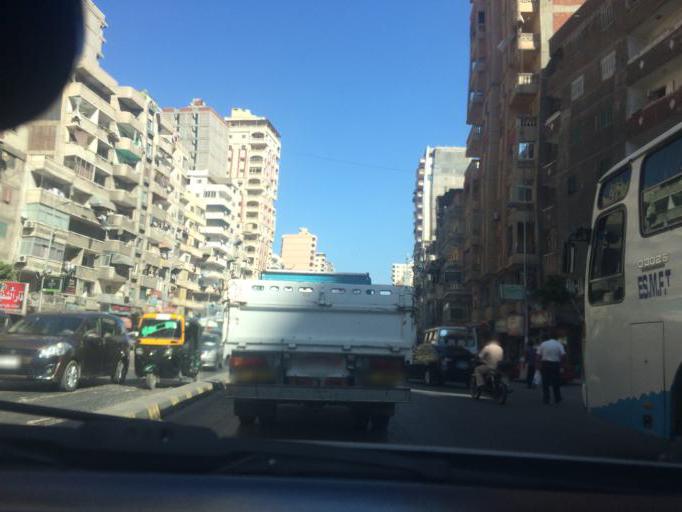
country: EG
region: Alexandria
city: Alexandria
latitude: 31.2654
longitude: 30.0034
